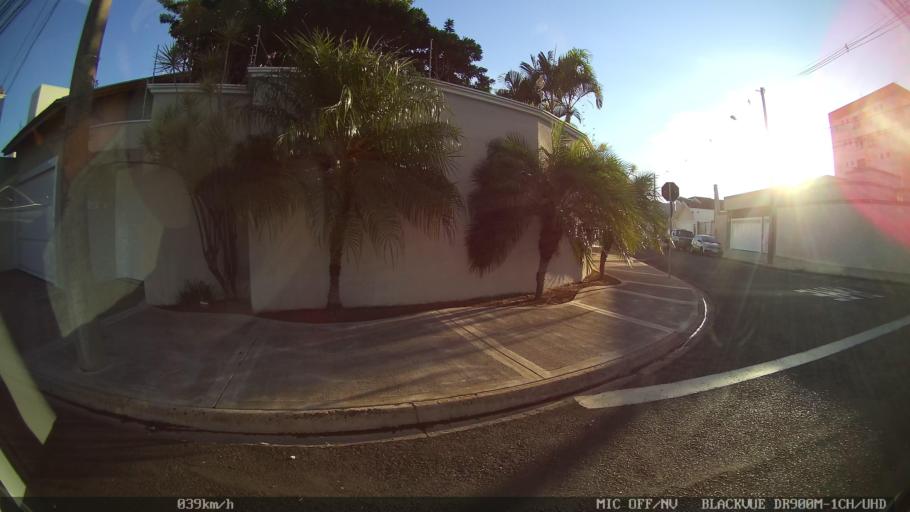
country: BR
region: Sao Paulo
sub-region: Franca
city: Franca
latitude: -20.5079
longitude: -47.3965
